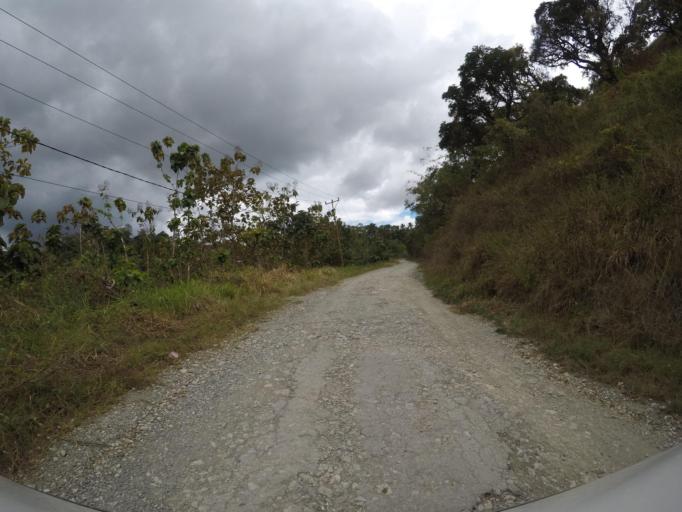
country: TL
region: Baucau
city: Baucau
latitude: -8.6213
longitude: 126.6570
